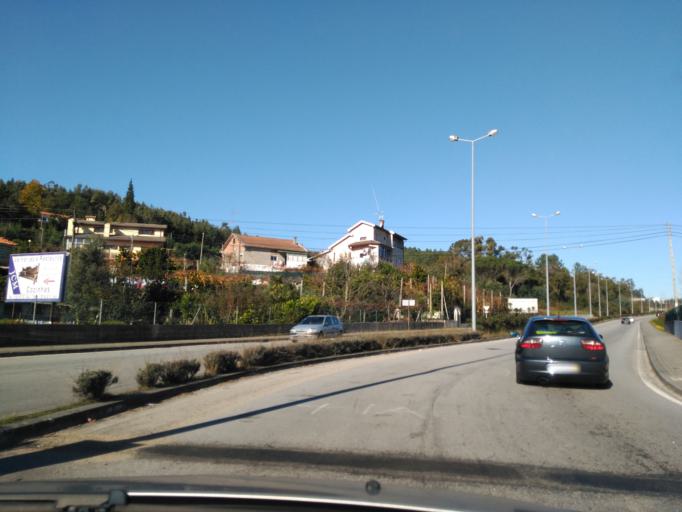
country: PT
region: Braga
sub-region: Braga
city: Adaufe
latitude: 41.5737
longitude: -8.3687
